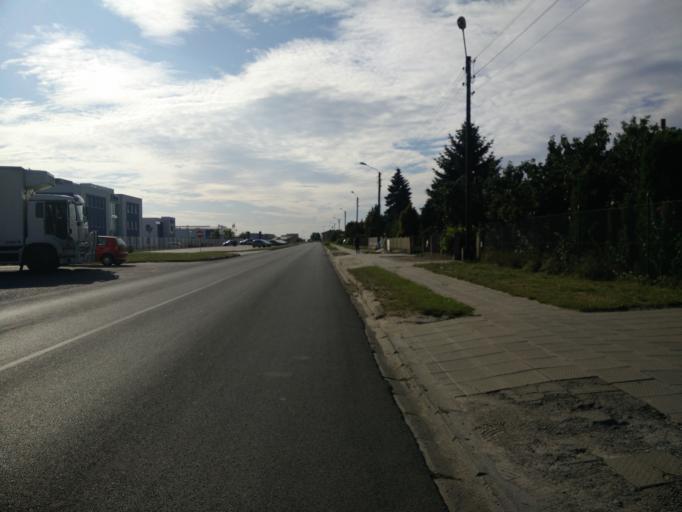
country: PL
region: Greater Poland Voivodeship
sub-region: Powiat sredzki
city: Sroda Wielkopolska
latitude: 52.2305
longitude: 17.2577
